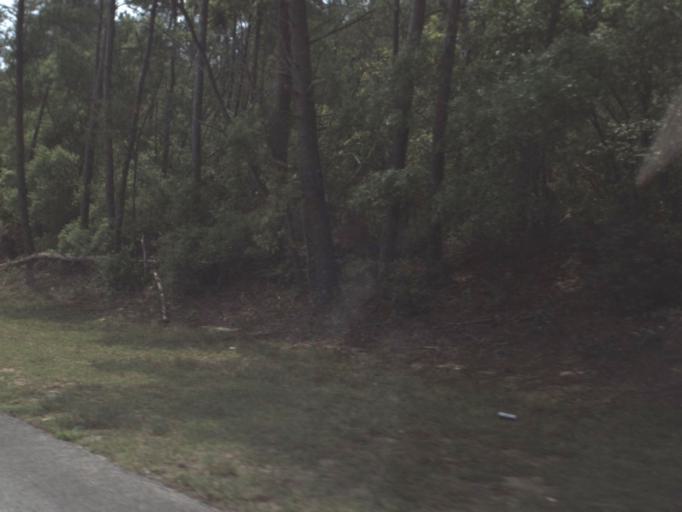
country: US
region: Florida
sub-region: Putnam County
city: Crescent City
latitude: 29.3326
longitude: -81.7152
